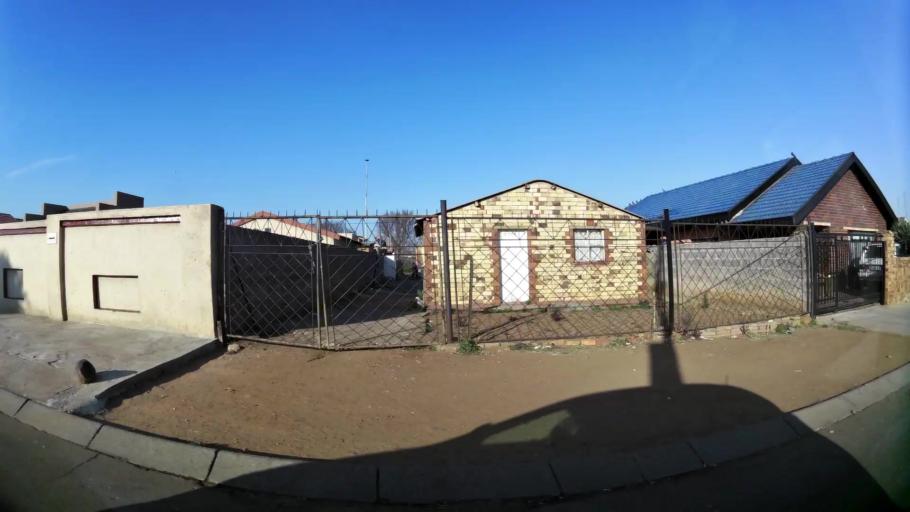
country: ZA
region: Gauteng
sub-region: City of Johannesburg Metropolitan Municipality
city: Soweto
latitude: -26.2614
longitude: 27.8842
